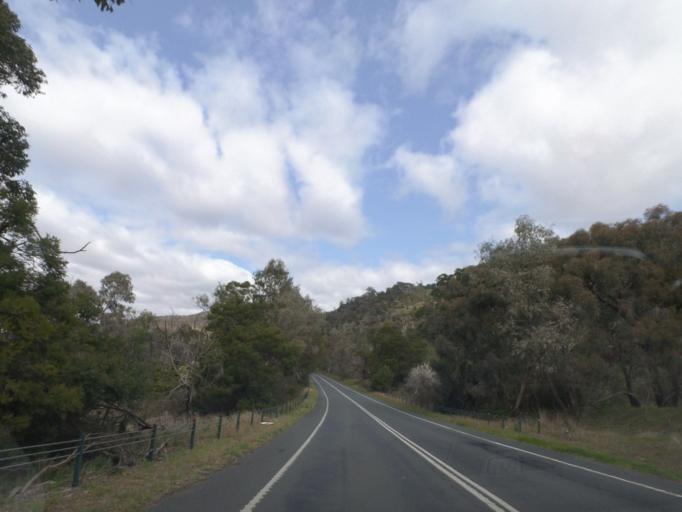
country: AU
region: Victoria
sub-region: Murrindindi
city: Kinglake West
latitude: -37.1080
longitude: 145.2071
